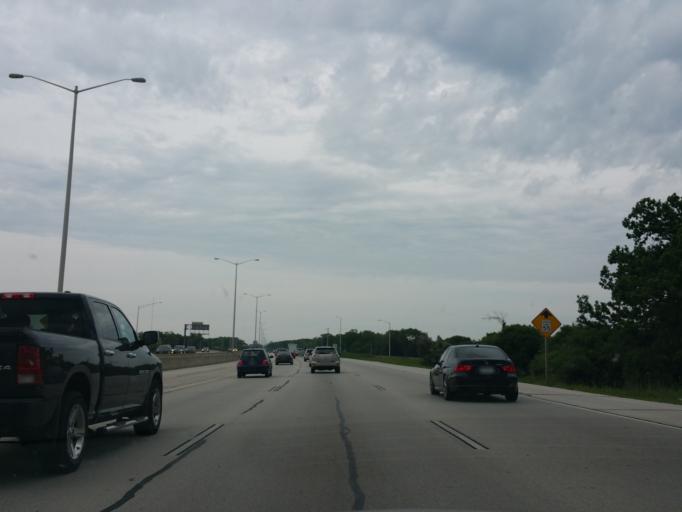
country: US
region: Wisconsin
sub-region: Waukesha County
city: Brookfield
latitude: 43.0244
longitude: -88.1113
